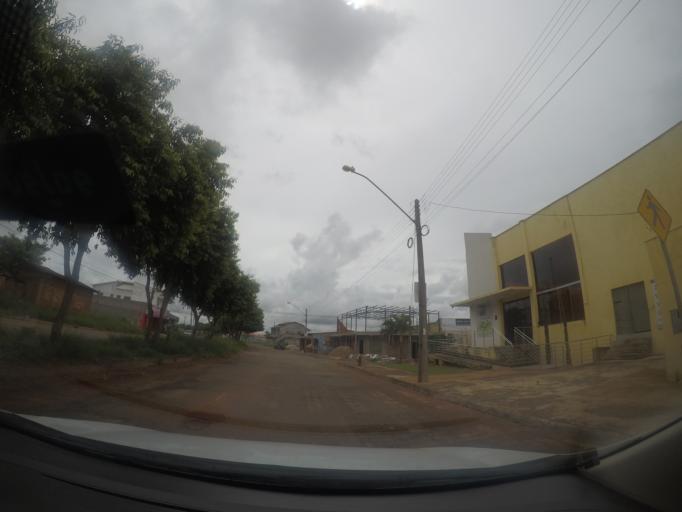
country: BR
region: Goias
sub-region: Trindade
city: Trindade
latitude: -16.6913
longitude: -49.3893
